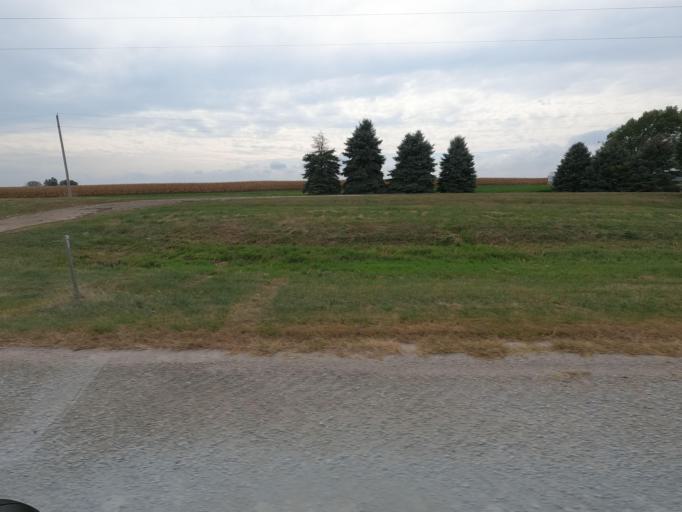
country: US
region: Iowa
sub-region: Marion County
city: Pella
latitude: 41.4421
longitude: -93.0116
